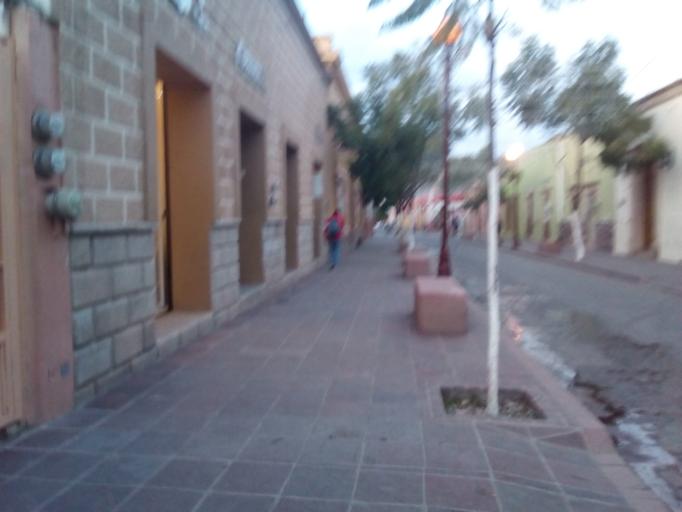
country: MX
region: Guanajuato
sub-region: San Luis de la Paz
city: San Luis de la Paz
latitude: 21.2996
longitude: -100.5148
